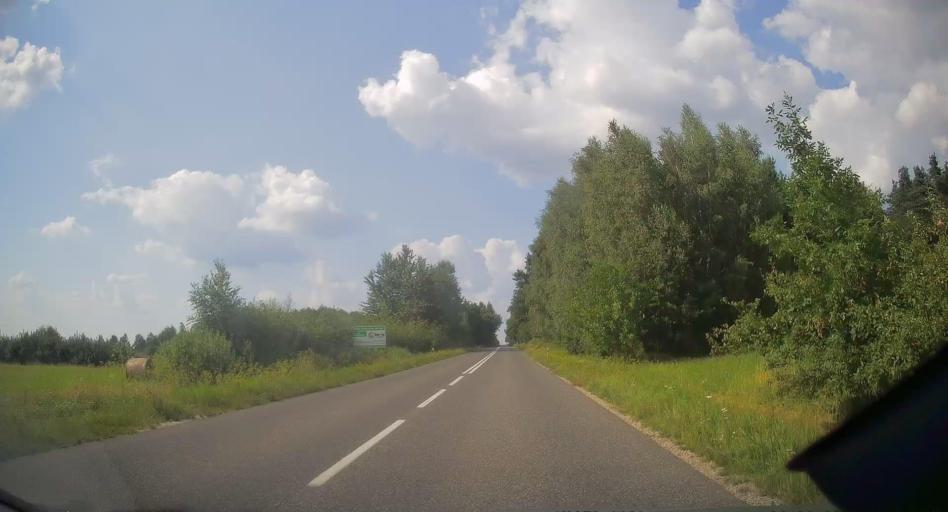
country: PL
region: Swietokrzyskie
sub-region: Powiat kielecki
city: Lopuszno
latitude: 50.9252
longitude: 20.2399
